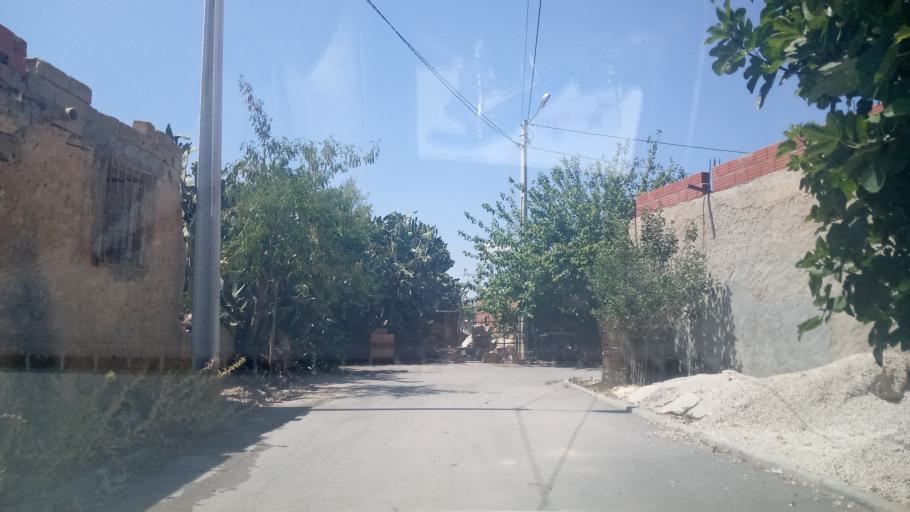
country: TN
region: Al Qayrawan
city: Sbikha
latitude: 36.1178
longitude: 10.0879
